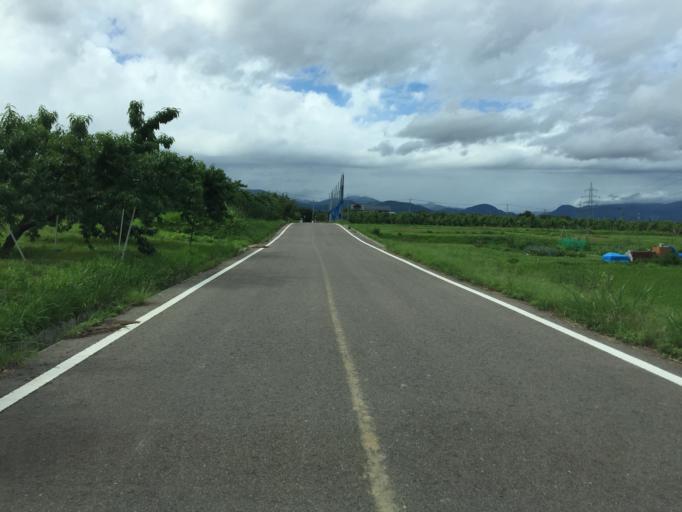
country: JP
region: Fukushima
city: Fukushima-shi
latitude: 37.7294
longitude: 140.4109
